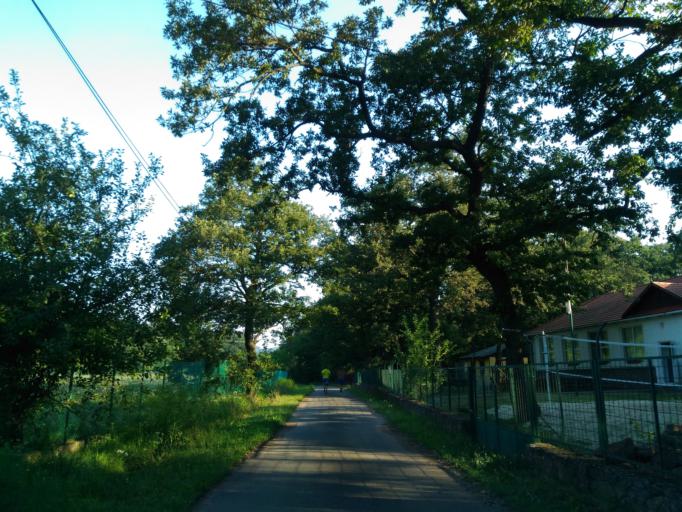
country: HU
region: Veszprem
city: Zanka
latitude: 46.8629
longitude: 17.6677
